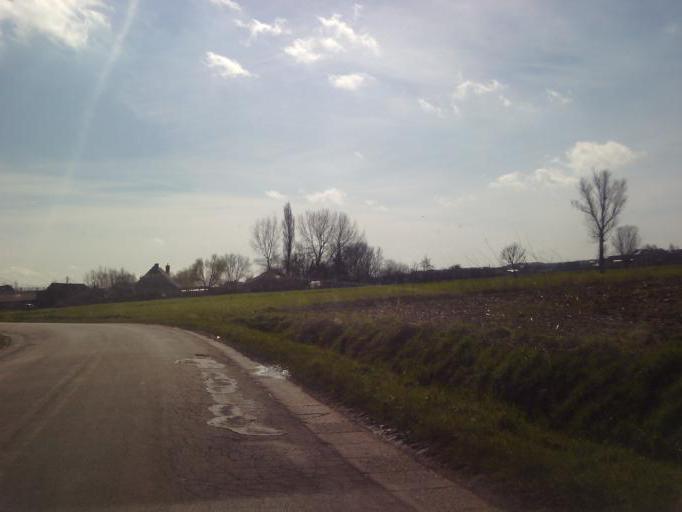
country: BE
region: Flanders
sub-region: Provincie Oost-Vlaanderen
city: Lokeren
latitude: 51.0712
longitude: 3.9960
